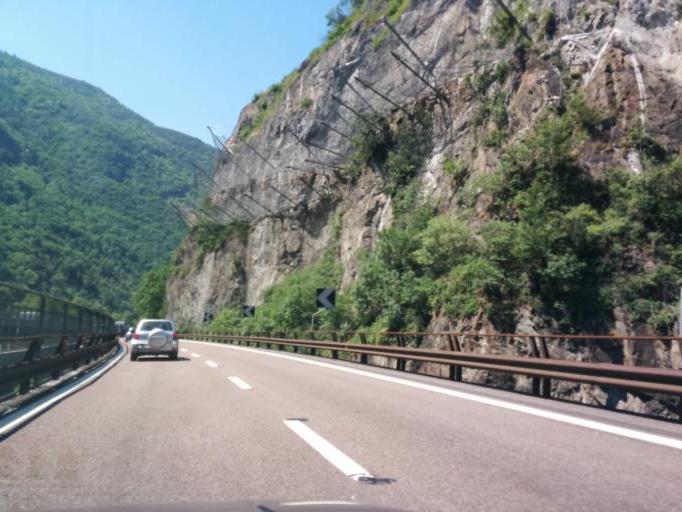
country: IT
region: Trentino-Alto Adige
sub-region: Bolzano
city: Cornedo All'Isarco
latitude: 46.4928
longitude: 11.4338
